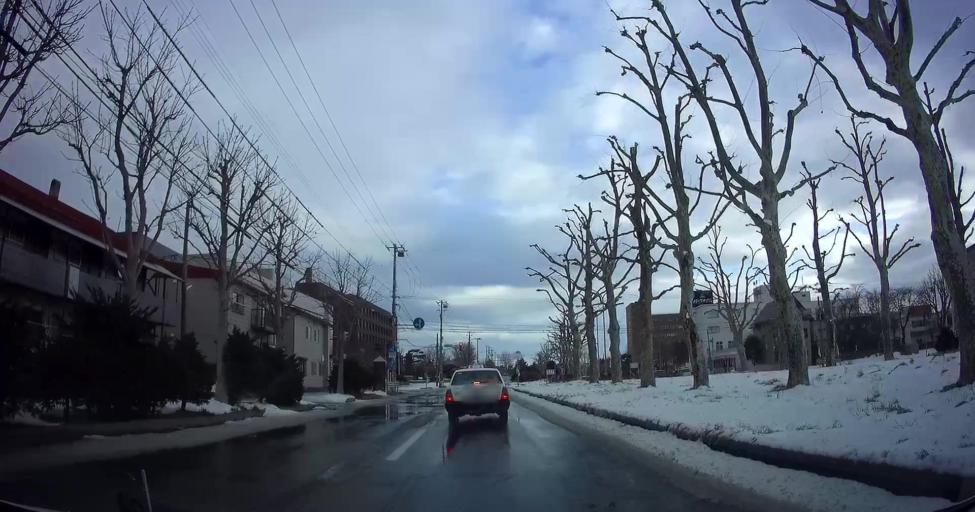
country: JP
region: Hokkaido
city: Hakodate
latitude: 41.7789
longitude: 140.7369
